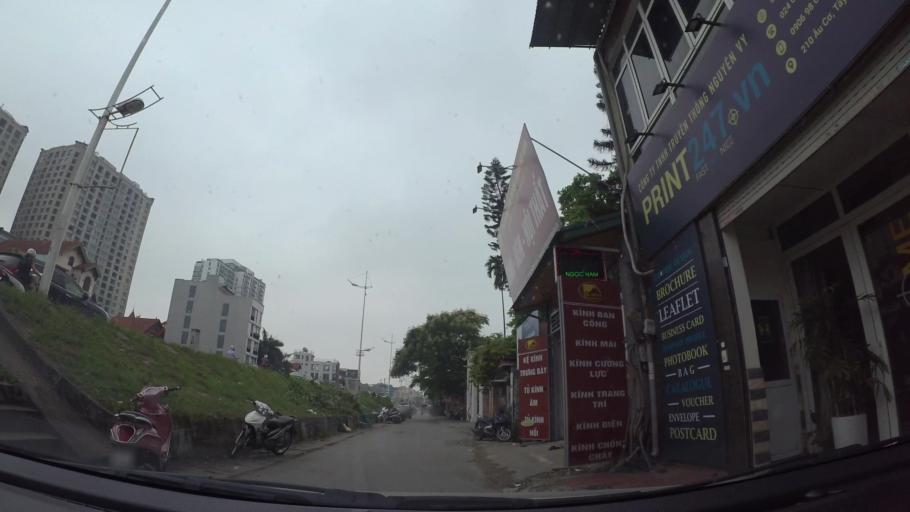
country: VN
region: Ha Noi
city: Tay Ho
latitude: 21.0667
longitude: 105.8293
